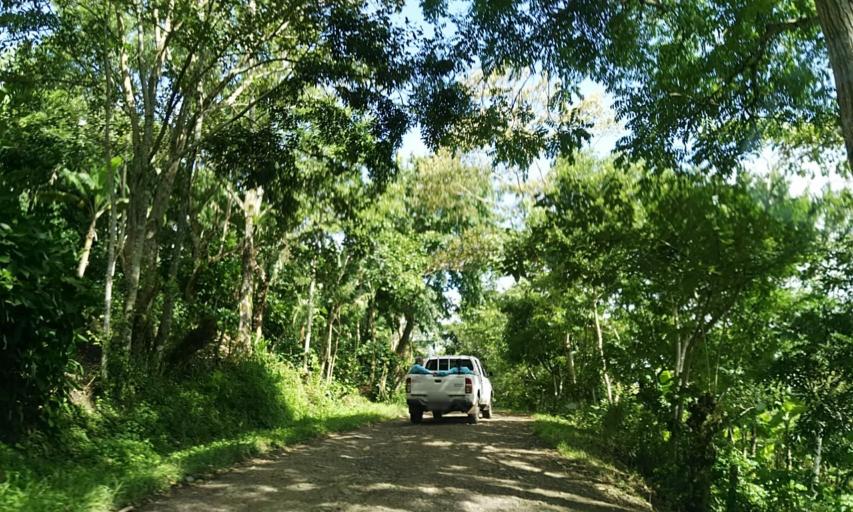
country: NI
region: Matagalpa
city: San Ramon
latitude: 12.9920
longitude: -85.8618
